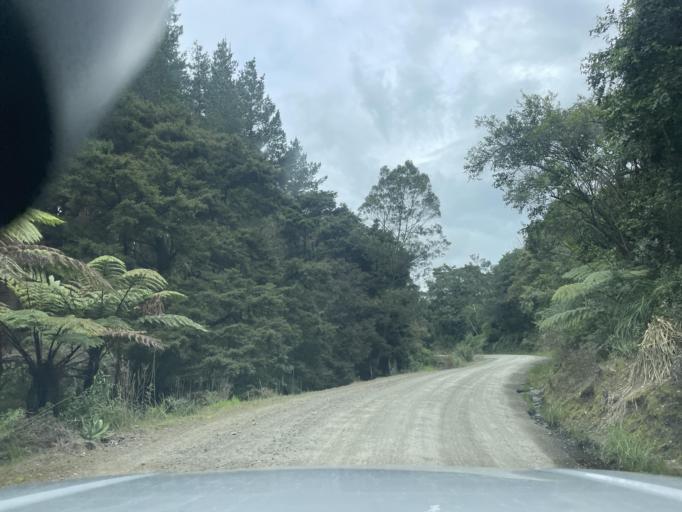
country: NZ
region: Northland
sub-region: Kaipara District
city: Dargaville
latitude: -35.8293
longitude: 173.8267
